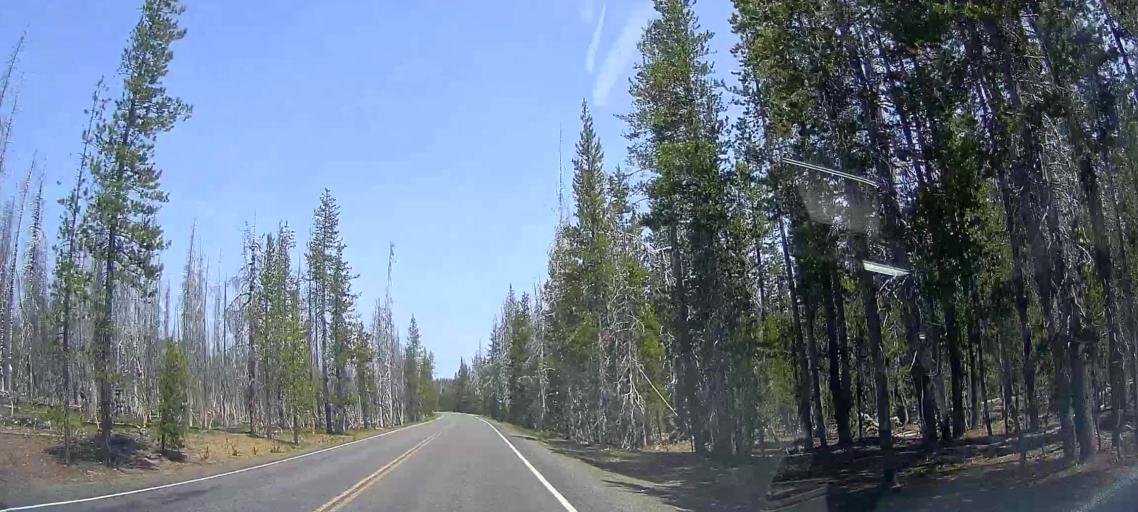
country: US
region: Oregon
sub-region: Lane County
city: Oakridge
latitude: 43.0419
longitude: -122.1176
